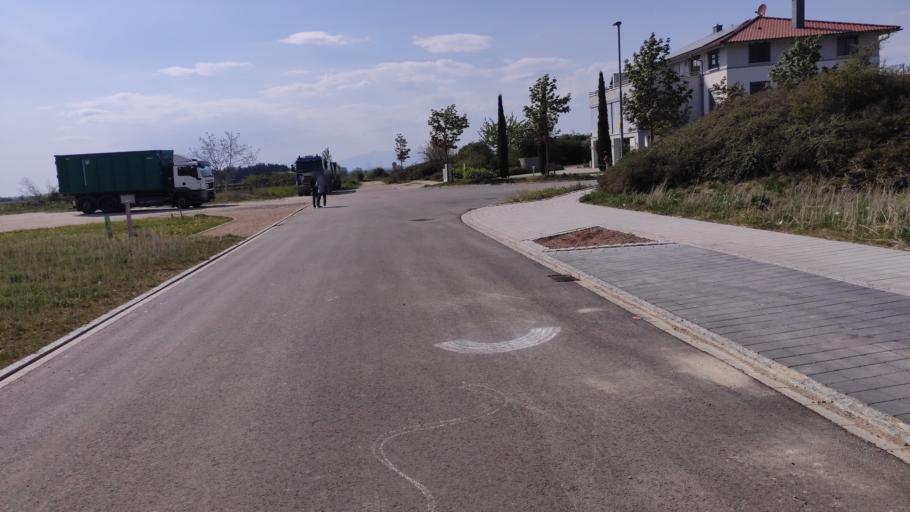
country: DE
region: Baden-Wuerttemberg
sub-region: Freiburg Region
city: Bad Krozingen
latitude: 47.8852
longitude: 7.7201
